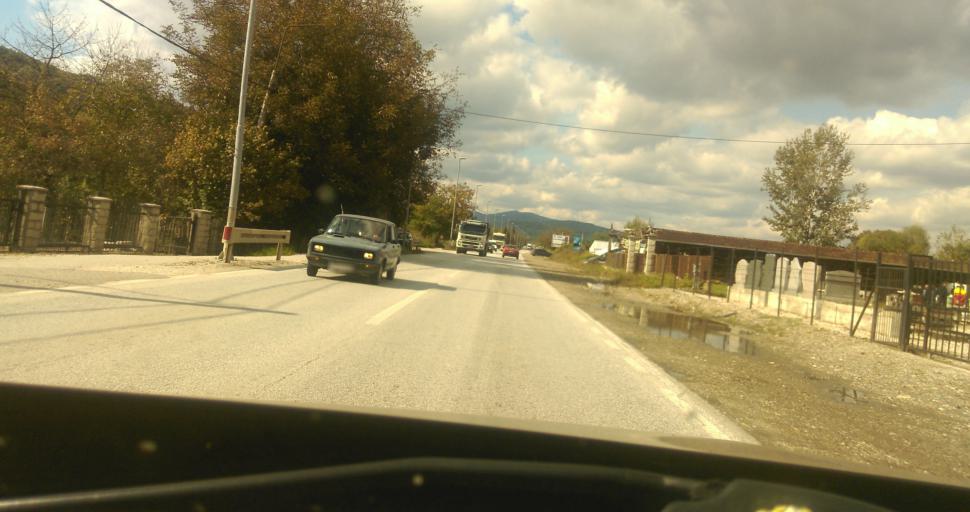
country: RS
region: Central Serbia
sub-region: Moravicki Okrug
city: Cacak
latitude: 43.8929
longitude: 20.3050
